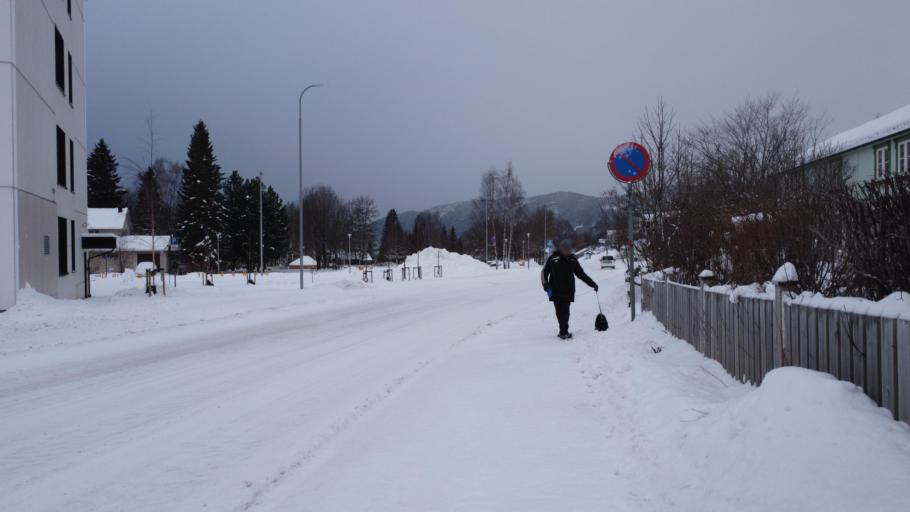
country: NO
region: Nordland
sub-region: Rana
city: Mo i Rana
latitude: 66.3125
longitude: 14.1466
